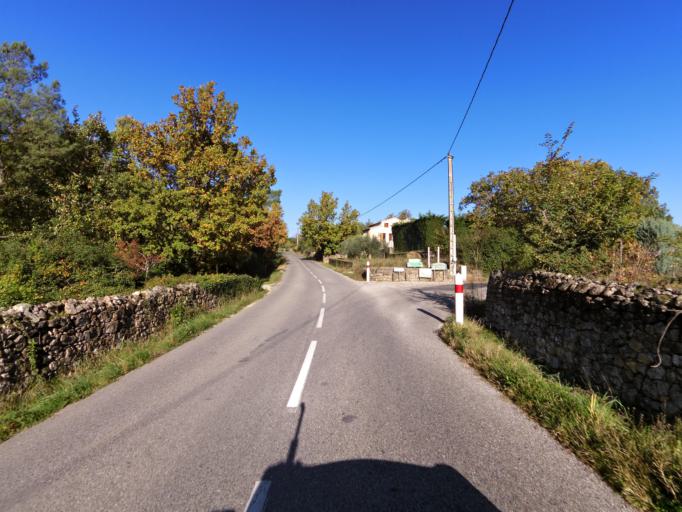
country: FR
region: Rhone-Alpes
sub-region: Departement de l'Ardeche
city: Lablachere
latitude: 44.4703
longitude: 4.2028
